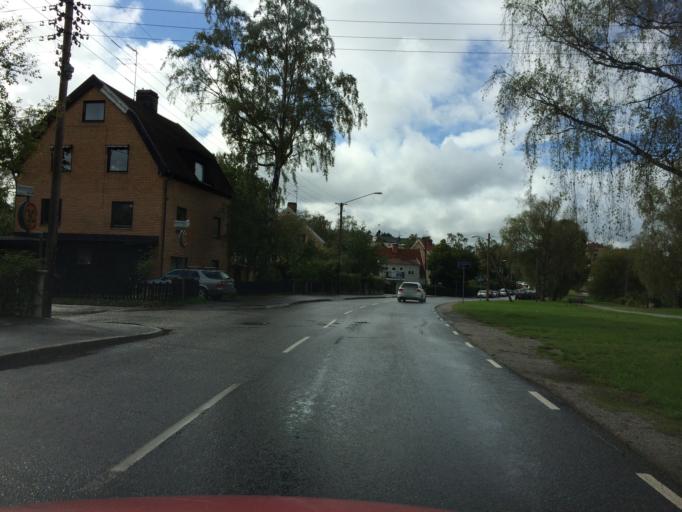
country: SE
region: Stockholm
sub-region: Huddinge Kommun
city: Segeltorp
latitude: 59.3005
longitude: 17.9621
